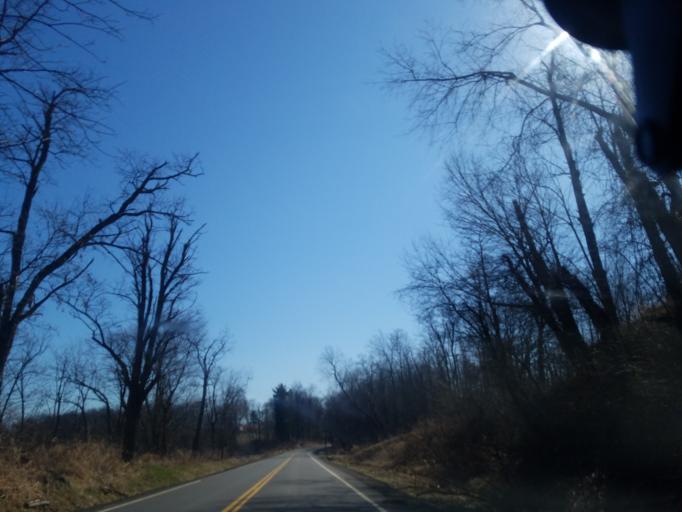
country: US
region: Ohio
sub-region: Tuscarawas County
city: Rockford
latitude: 40.5625
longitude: -81.3381
